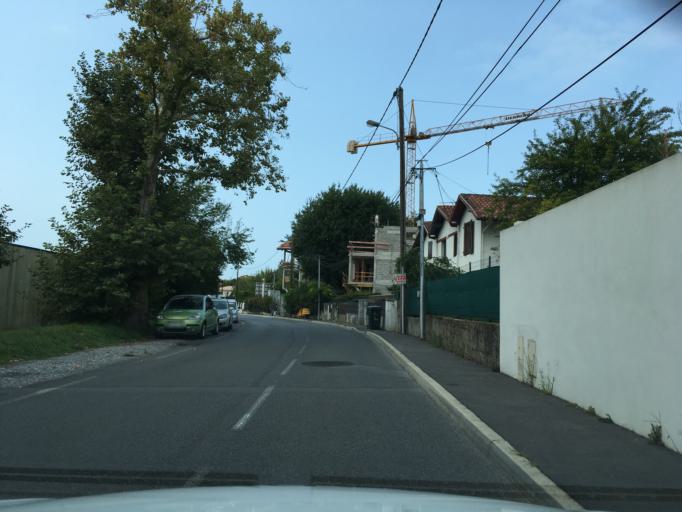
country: FR
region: Aquitaine
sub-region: Departement des Pyrenees-Atlantiques
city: Anglet
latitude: 43.4856
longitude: -1.5067
